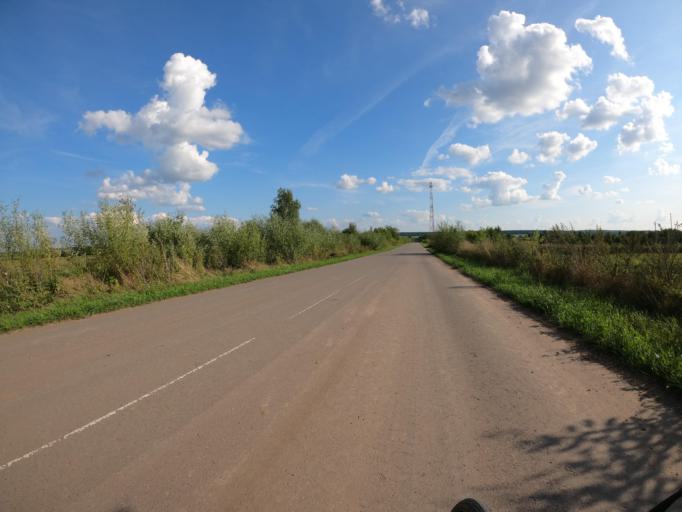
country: RU
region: Moskovskaya
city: Troitskoye
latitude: 55.2000
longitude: 38.4888
